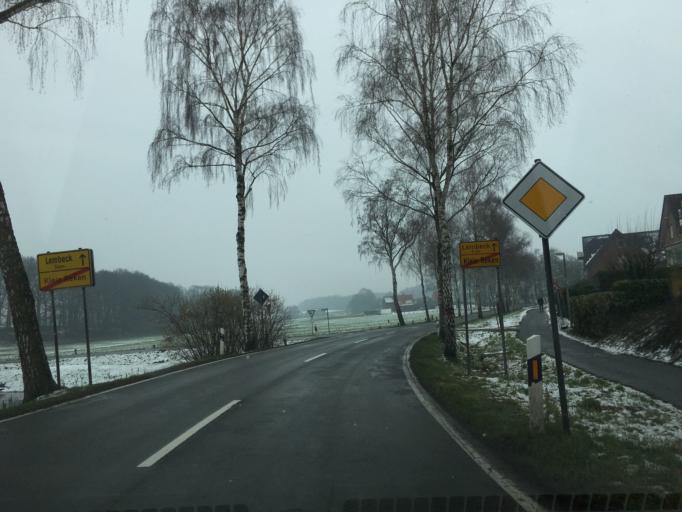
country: DE
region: North Rhine-Westphalia
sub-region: Regierungsbezirk Munster
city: Klein Reken
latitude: 51.7844
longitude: 7.0374
